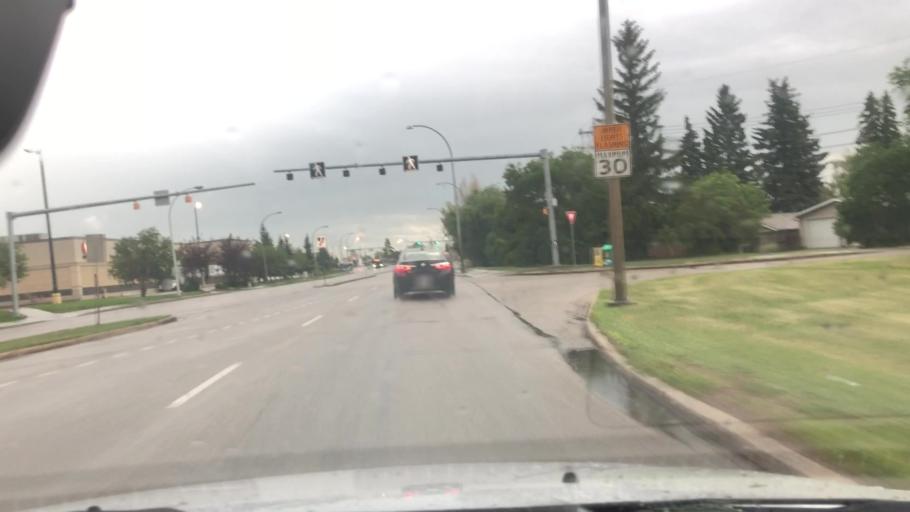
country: CA
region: Alberta
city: Edmonton
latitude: 53.5383
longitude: -113.4272
